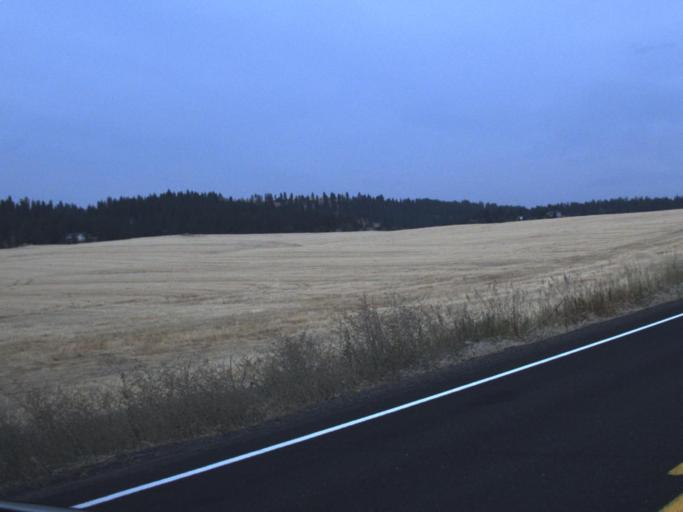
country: US
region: Washington
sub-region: Spokane County
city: Mead
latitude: 47.7875
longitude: -117.2933
